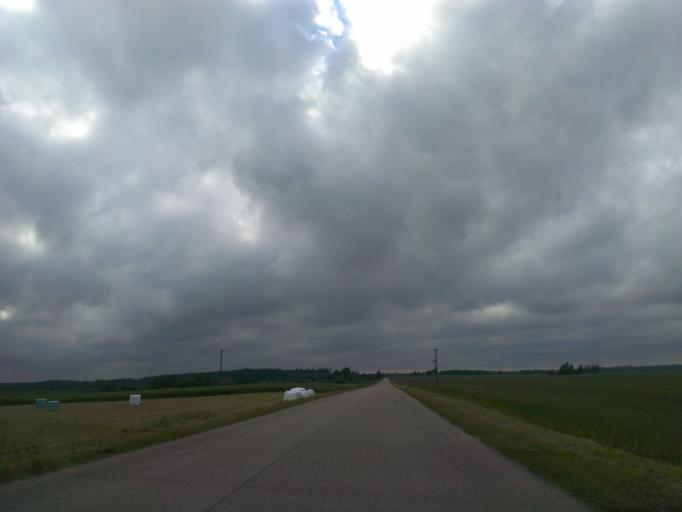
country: LV
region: Aizpute
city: Aizpute
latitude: 56.7141
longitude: 21.4706
